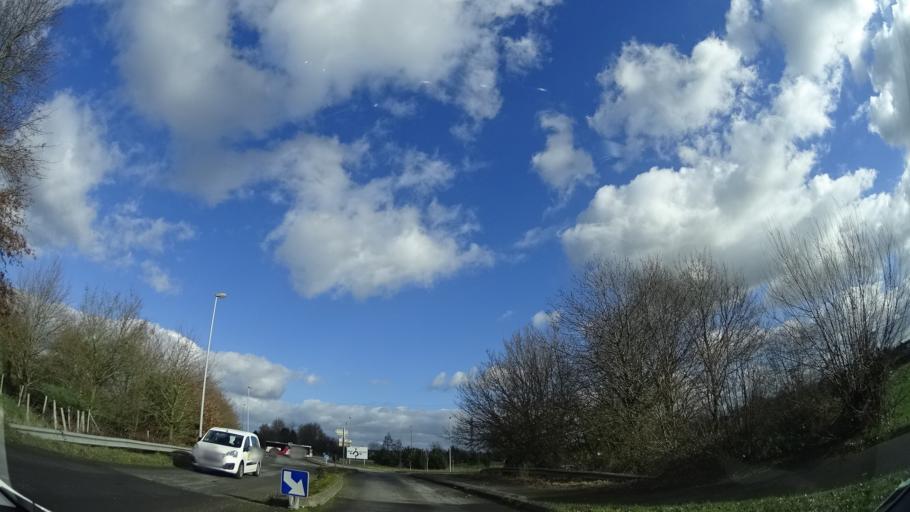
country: FR
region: Brittany
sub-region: Departement d'Ille-et-Vilaine
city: Chantepie
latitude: 48.0769
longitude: -1.6338
